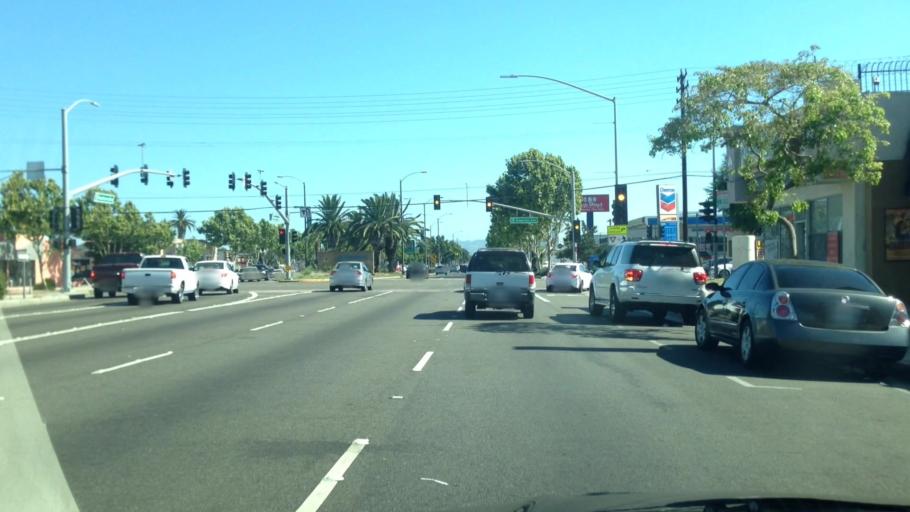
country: US
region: California
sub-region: Los Angeles County
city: Hawthorne
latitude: 33.9026
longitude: -118.3528
